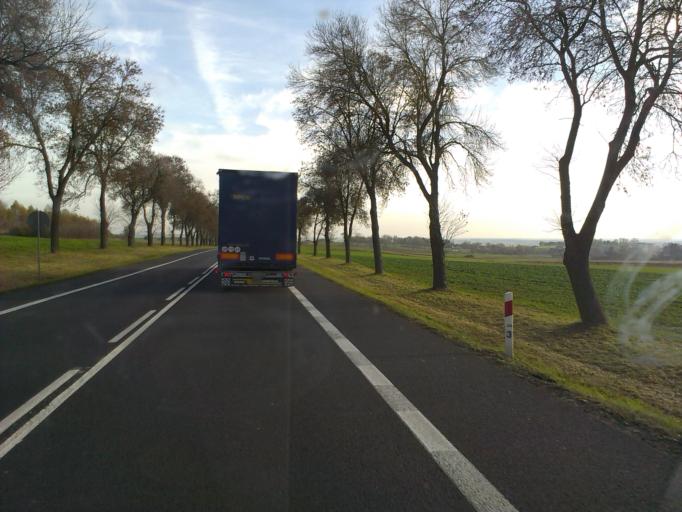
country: PL
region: Lower Silesian Voivodeship
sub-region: Powiat polkowicki
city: Gaworzyce
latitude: 51.6412
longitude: 15.8799
